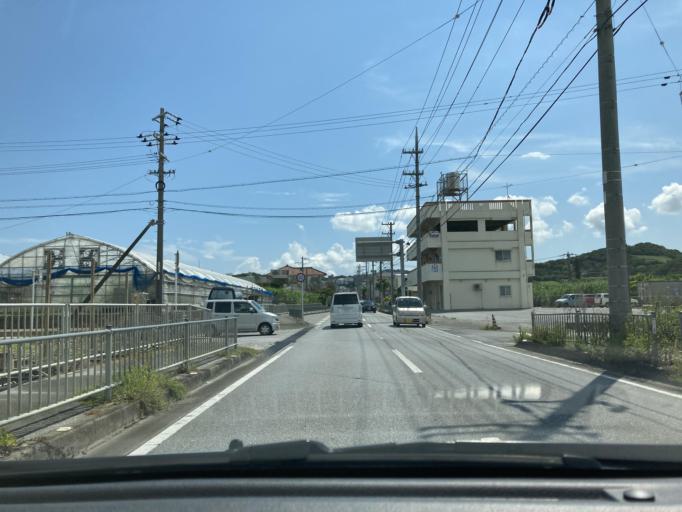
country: JP
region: Okinawa
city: Tomigusuku
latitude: 26.1826
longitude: 127.7370
